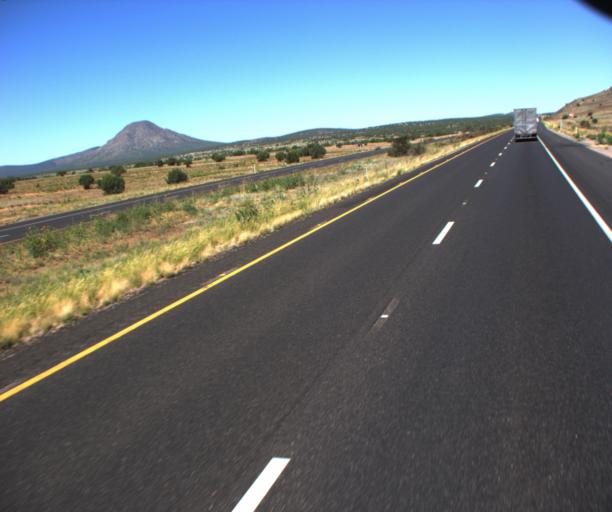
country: US
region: Arizona
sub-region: Yavapai County
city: Paulden
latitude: 35.2420
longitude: -112.6679
